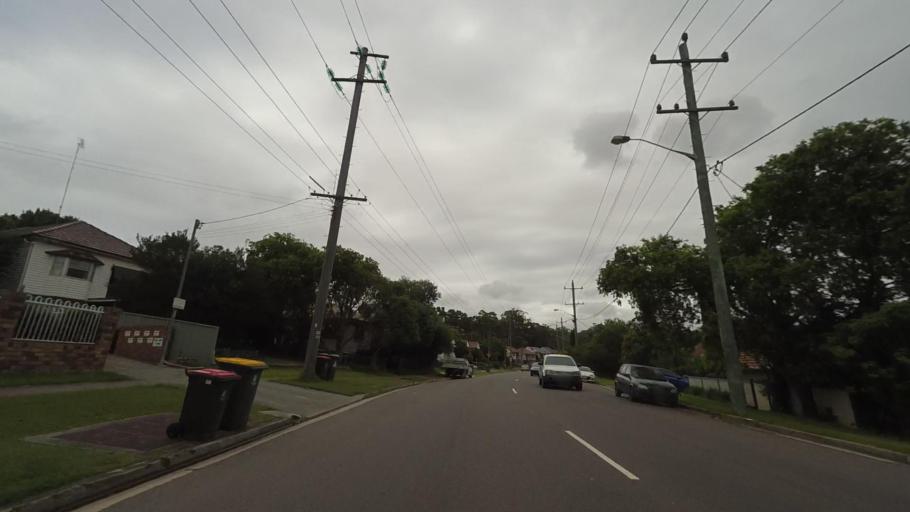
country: AU
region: New South Wales
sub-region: Lake Macquarie Shire
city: Kotara
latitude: -32.9445
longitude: 151.6939
